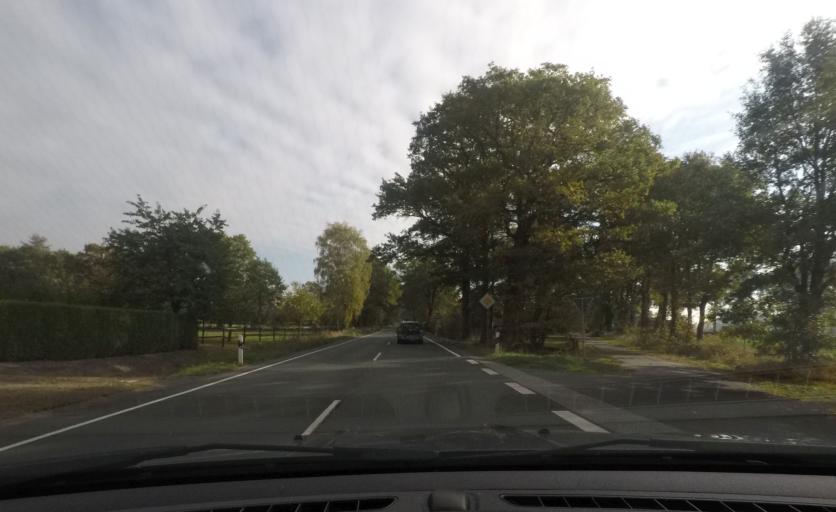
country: DE
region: North Rhine-Westphalia
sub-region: Regierungsbezirk Munster
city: Dulmen
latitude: 51.8480
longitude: 7.1854
